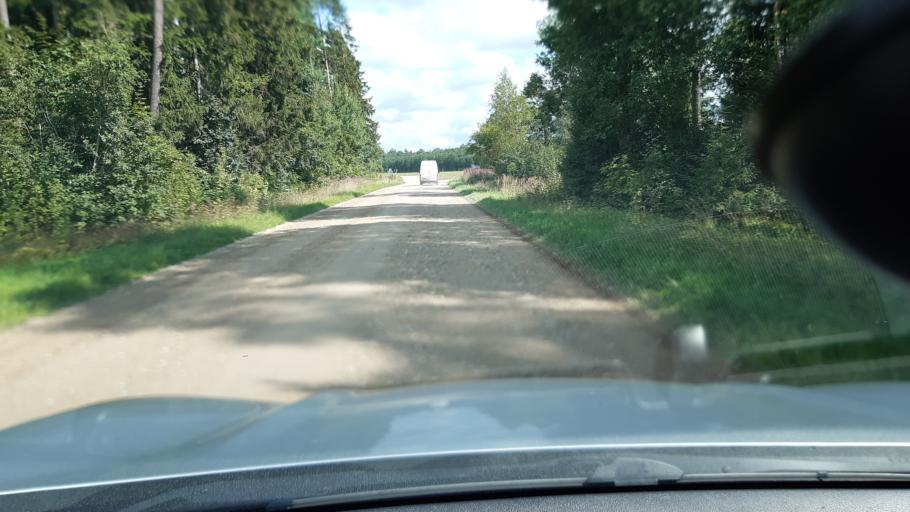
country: EE
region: Raplamaa
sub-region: Kehtna vald
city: Kehtna
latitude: 58.9088
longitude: 25.1403
